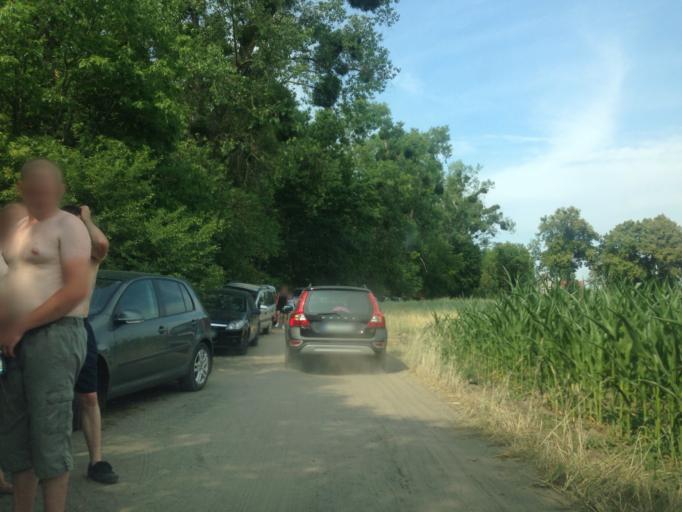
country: PL
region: Kujawsko-Pomorskie
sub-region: Powiat brodnicki
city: Bobrowo
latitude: 53.2576
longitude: 19.2977
